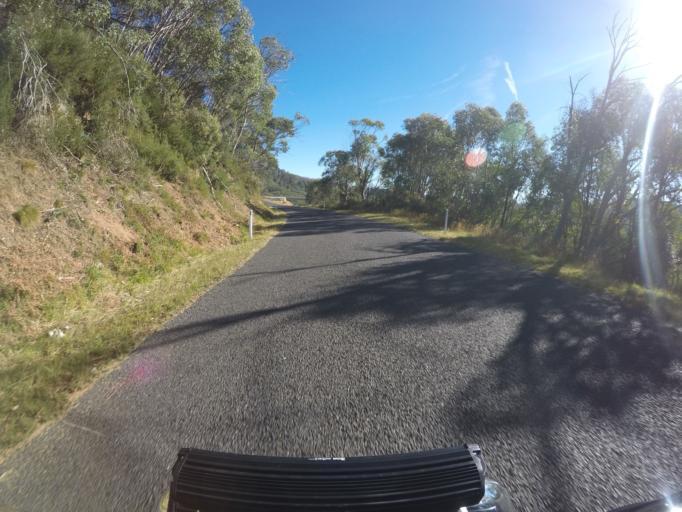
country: AU
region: New South Wales
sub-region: Snowy River
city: Jindabyne
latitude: -36.0533
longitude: 148.2729
